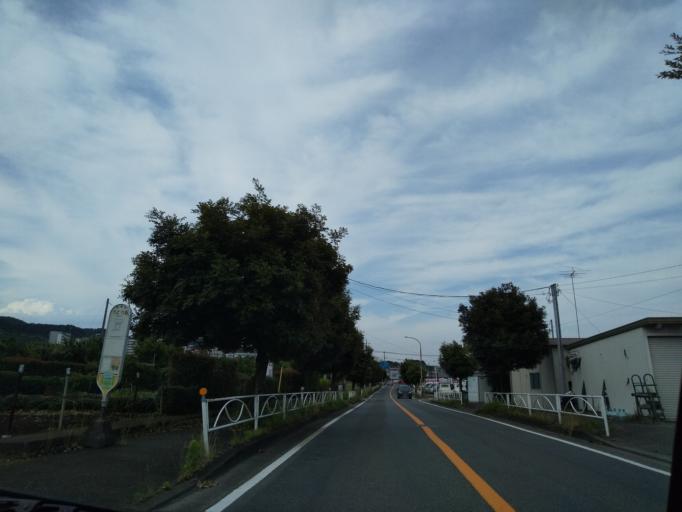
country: JP
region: Kanagawa
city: Atsugi
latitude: 35.4860
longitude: 139.3244
